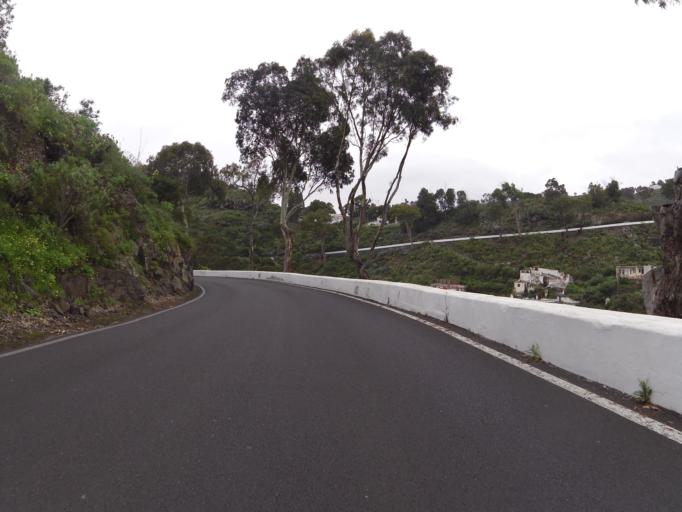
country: ES
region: Canary Islands
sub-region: Provincia de Las Palmas
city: Teror
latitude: 28.0786
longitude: -15.5164
